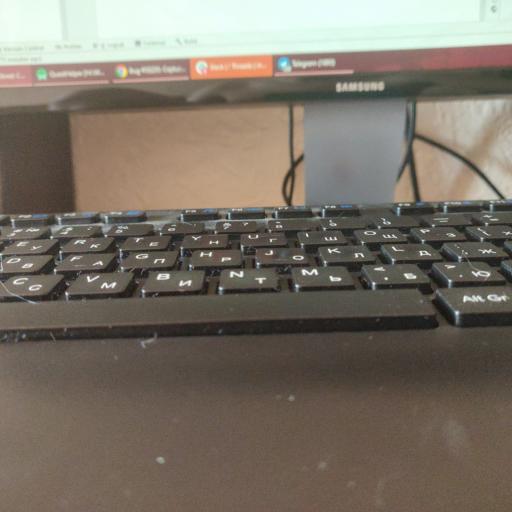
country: FI
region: Haeme
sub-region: Forssa
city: Jokioinen
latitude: 60.7861
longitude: 23.4724
